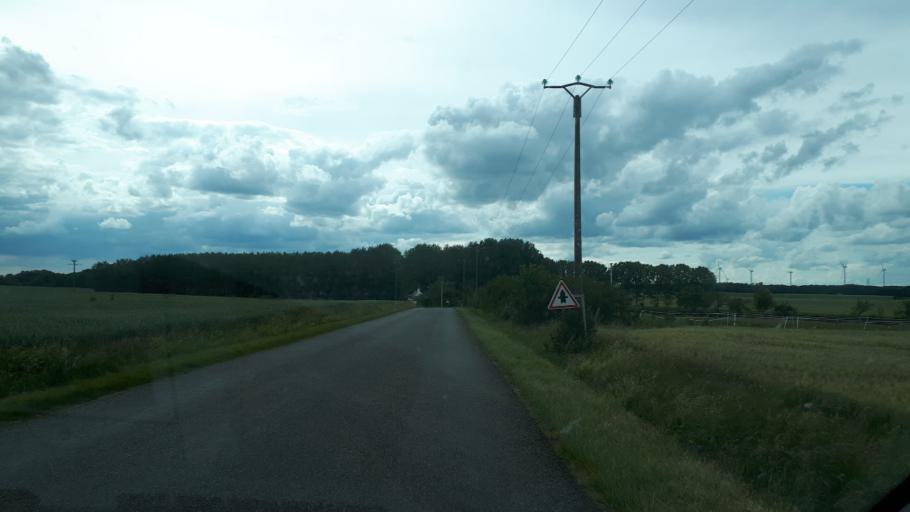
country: FR
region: Centre
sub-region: Departement de l'Indre
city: Reuilly
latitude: 47.0963
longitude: 1.9881
